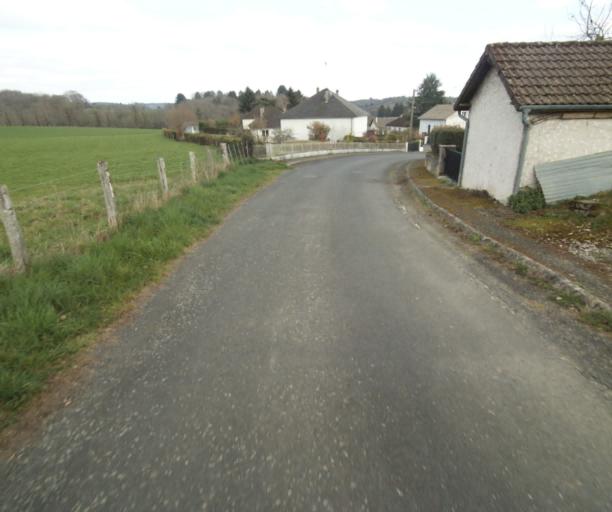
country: FR
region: Limousin
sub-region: Departement de la Correze
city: Saint-Clement
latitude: 45.3532
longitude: 1.6410
